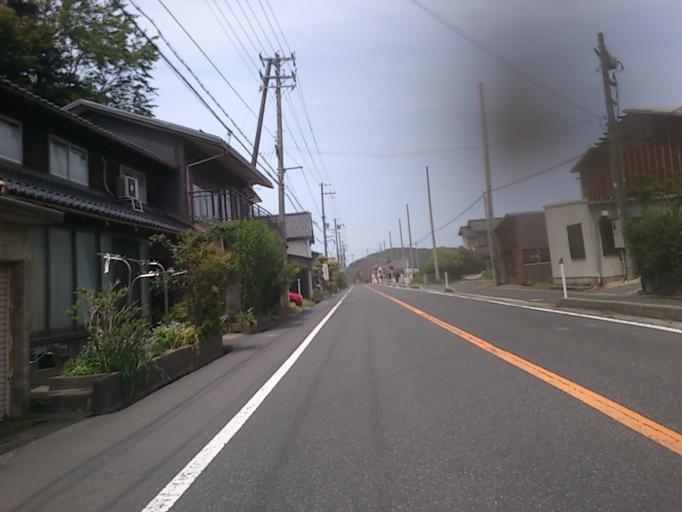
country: JP
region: Kyoto
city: Miyazu
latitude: 35.7181
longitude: 135.1042
